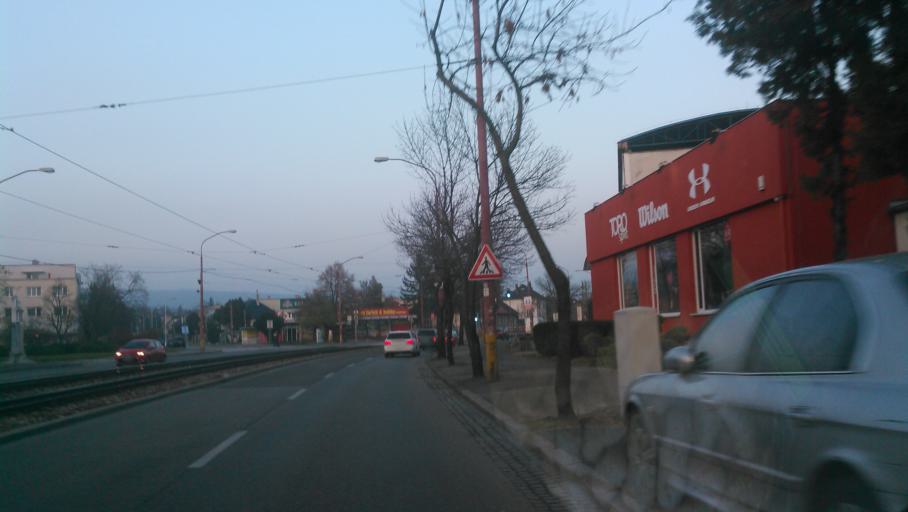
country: SK
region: Bratislavsky
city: Bratislava
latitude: 48.1811
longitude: 17.1293
